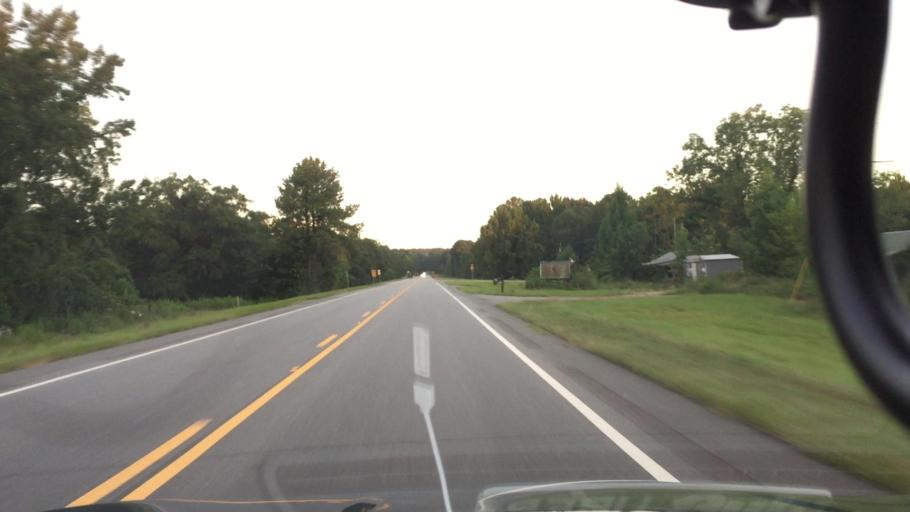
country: US
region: Alabama
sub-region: Coffee County
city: New Brockton
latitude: 31.4773
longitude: -85.9072
